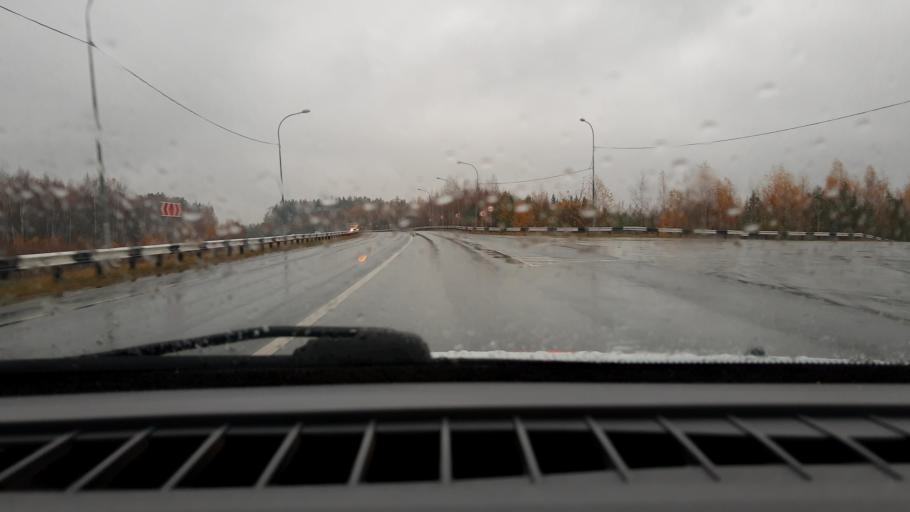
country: RU
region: Nizjnij Novgorod
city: Sitniki
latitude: 56.4695
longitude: 44.0365
